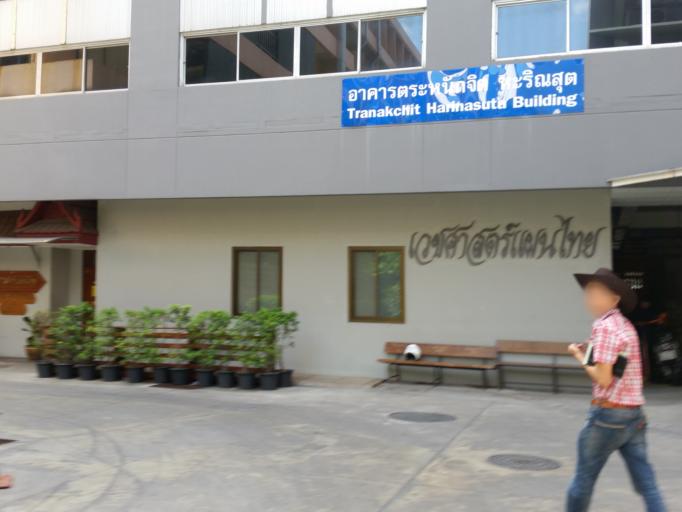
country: TH
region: Bangkok
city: Ratchathewi
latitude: 13.7659
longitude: 100.5341
